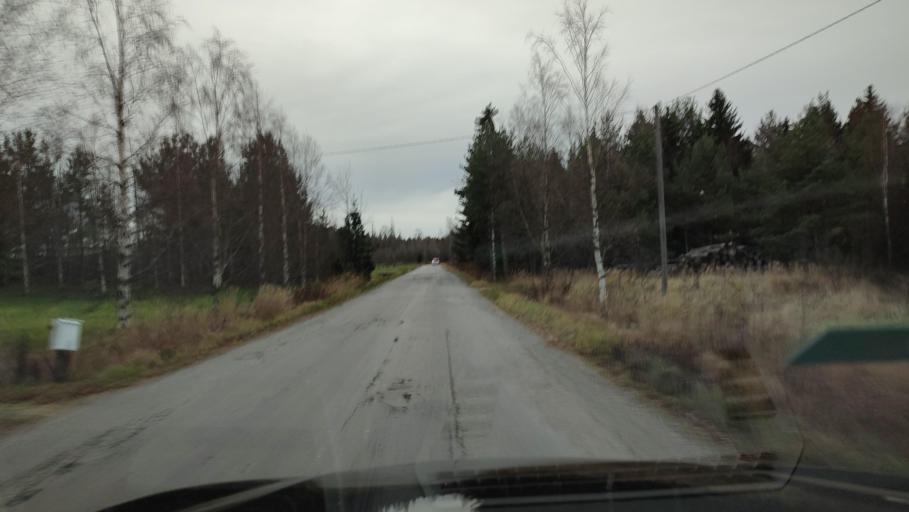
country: FI
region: Ostrobothnia
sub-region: Sydosterbotten
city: Naerpes
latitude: 62.4292
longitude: 21.4187
